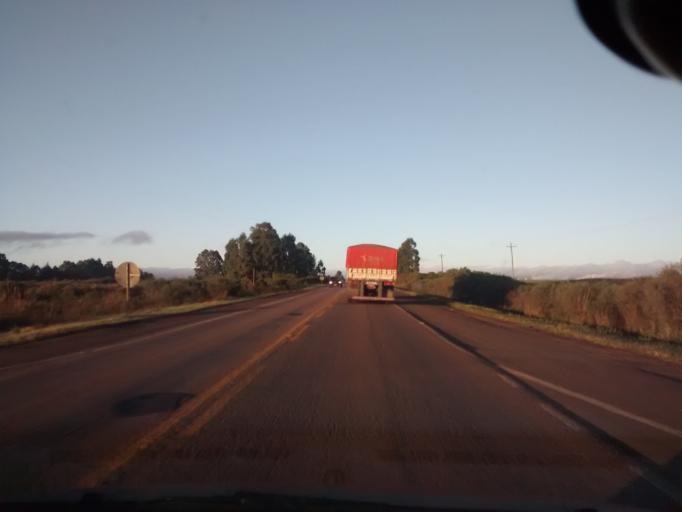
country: BR
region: Rio Grande do Sul
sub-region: Vacaria
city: Vacaria
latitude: -28.3991
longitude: -50.8523
